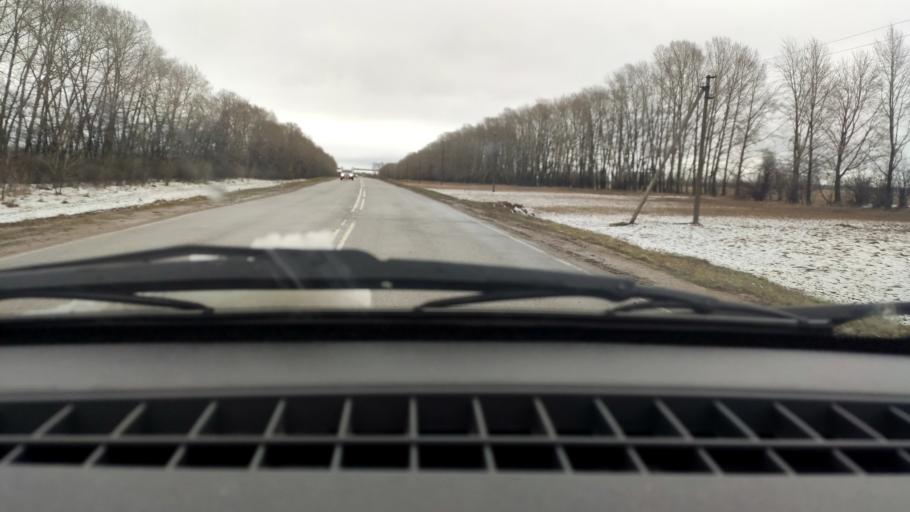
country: RU
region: Bashkortostan
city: Alekseyevka
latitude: 55.0640
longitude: 55.0980
